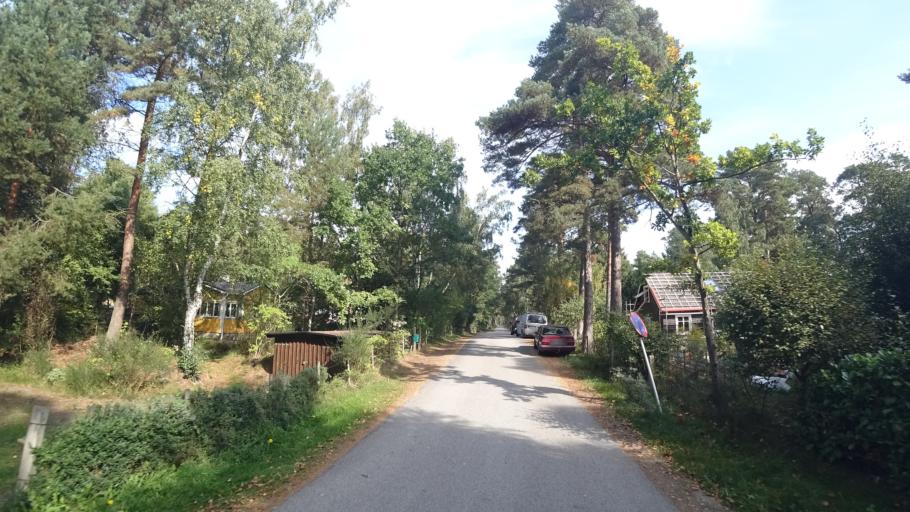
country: SE
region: Skane
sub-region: Kristianstads Kommun
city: Ahus
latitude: 55.9111
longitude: 14.3015
